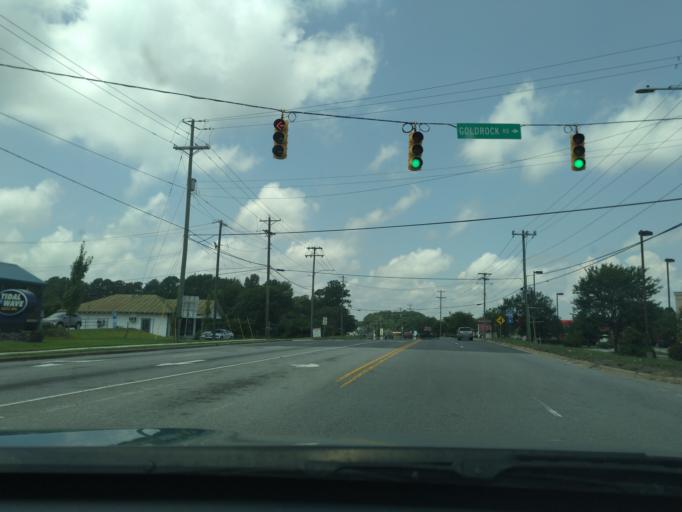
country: US
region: North Carolina
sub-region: Nash County
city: Rocky Mount
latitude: 35.9807
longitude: -77.8088
